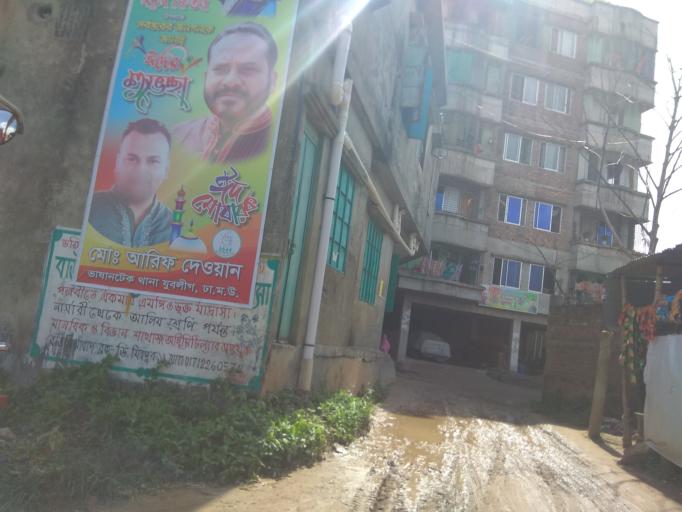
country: BD
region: Dhaka
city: Tungi
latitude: 23.8178
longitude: 90.3846
